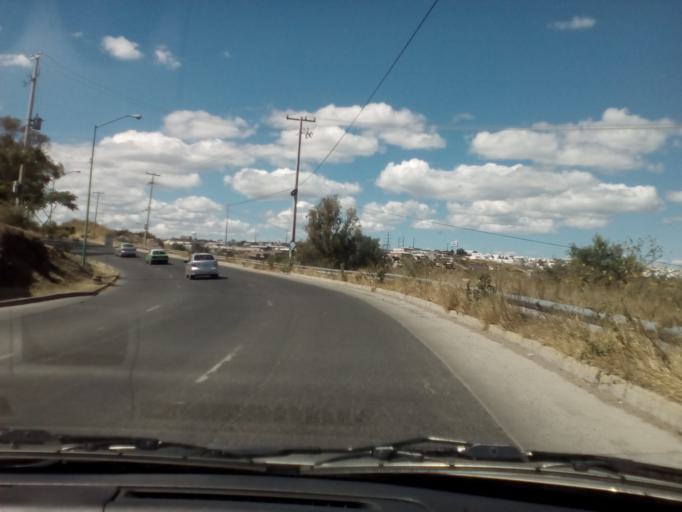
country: MX
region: Guanajuato
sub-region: Leon
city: La Ermita
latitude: 21.1356
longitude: -101.7170
